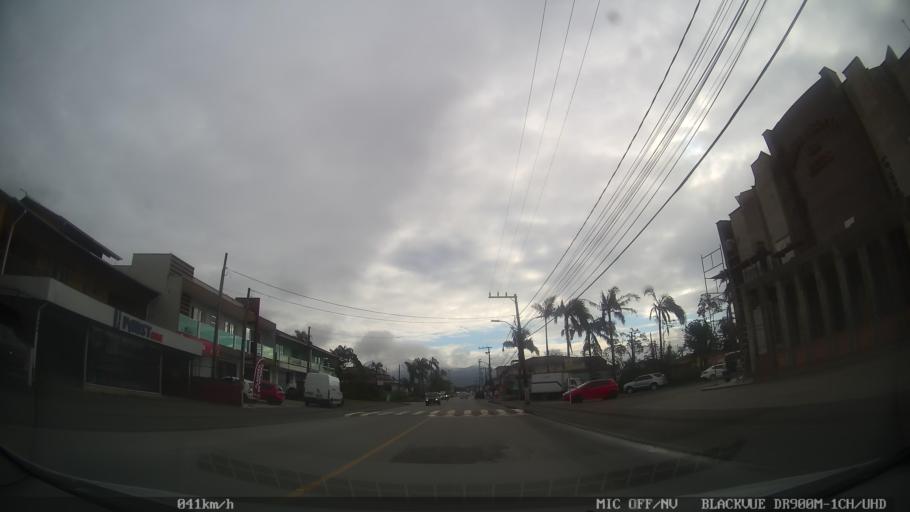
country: BR
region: Santa Catarina
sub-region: Joinville
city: Joinville
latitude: -26.0365
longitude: -48.8566
